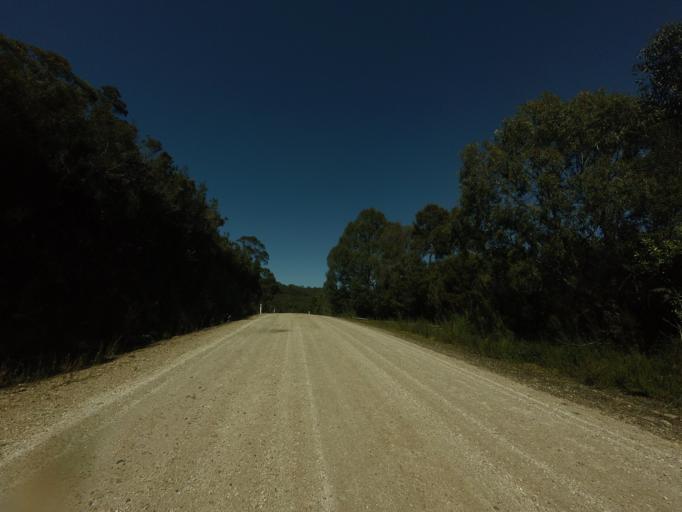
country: AU
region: Tasmania
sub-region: Huon Valley
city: Geeveston
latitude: -42.9786
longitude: 146.3666
